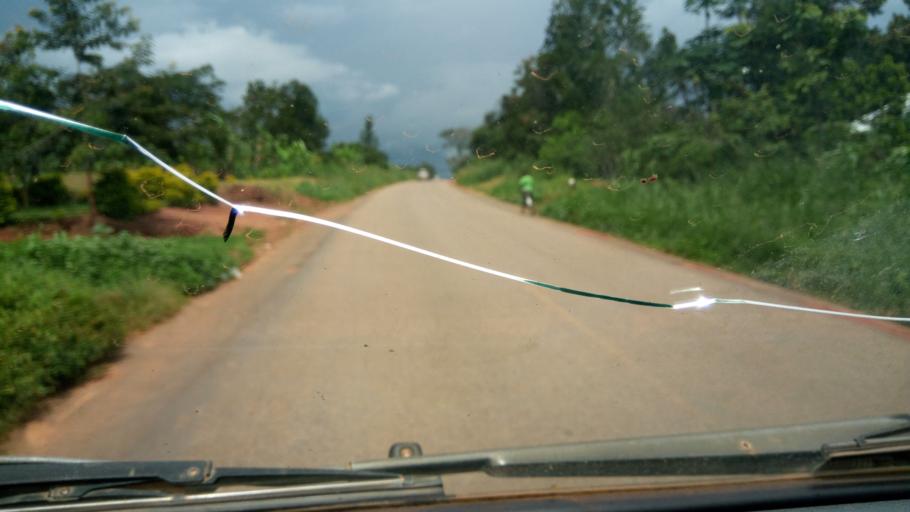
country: UG
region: Central Region
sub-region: Wakiso District
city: Wakiso
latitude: 0.5155
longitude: 32.2829
